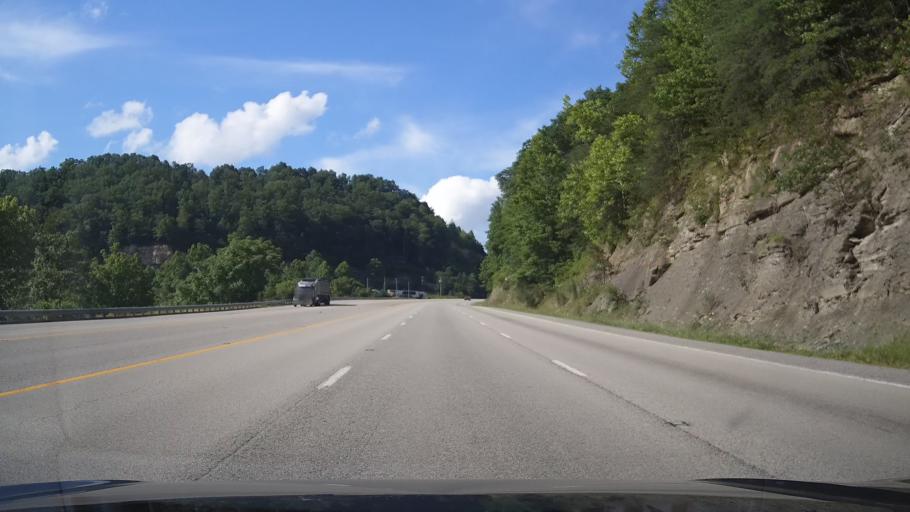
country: US
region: Kentucky
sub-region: Lawrence County
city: Louisa
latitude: 38.0315
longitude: -82.6523
